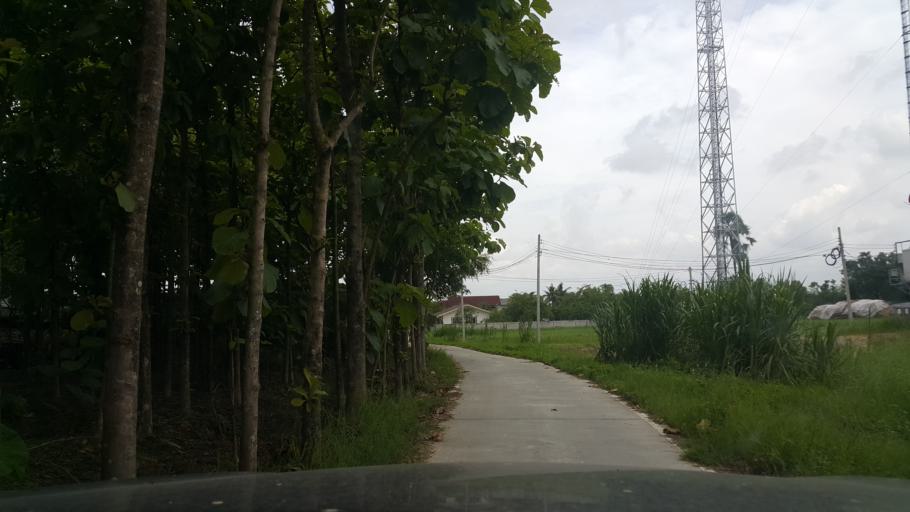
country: TH
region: Lamphun
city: Ban Thi
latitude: 18.6725
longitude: 99.1462
